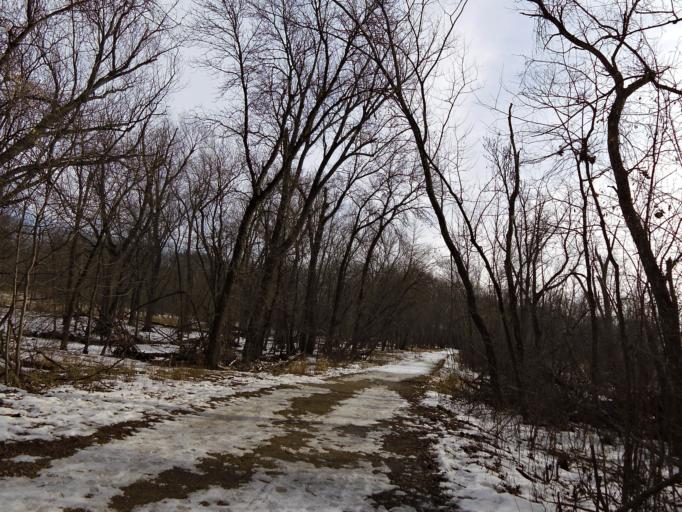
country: US
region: Minnesota
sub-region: Dakota County
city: Eagan
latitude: 44.8576
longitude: -93.2151
